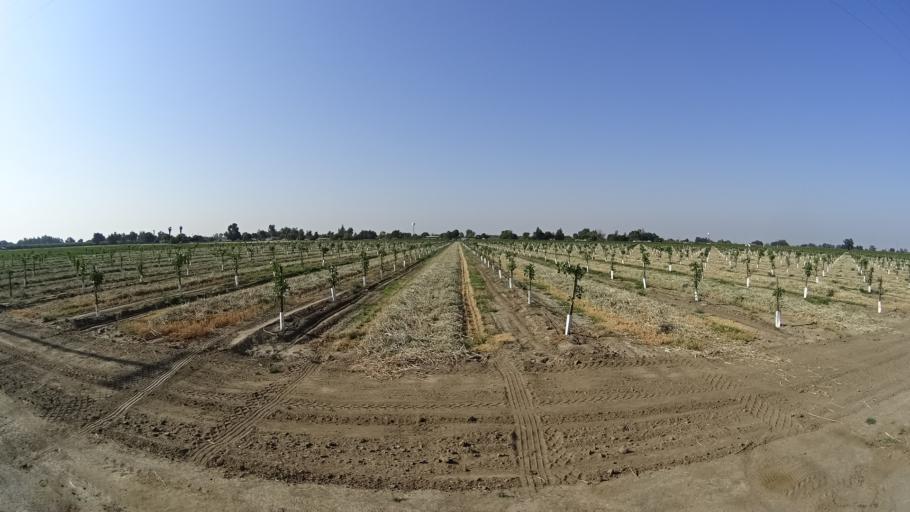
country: US
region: California
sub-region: Fresno County
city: Riverdale
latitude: 36.3585
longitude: -119.8394
